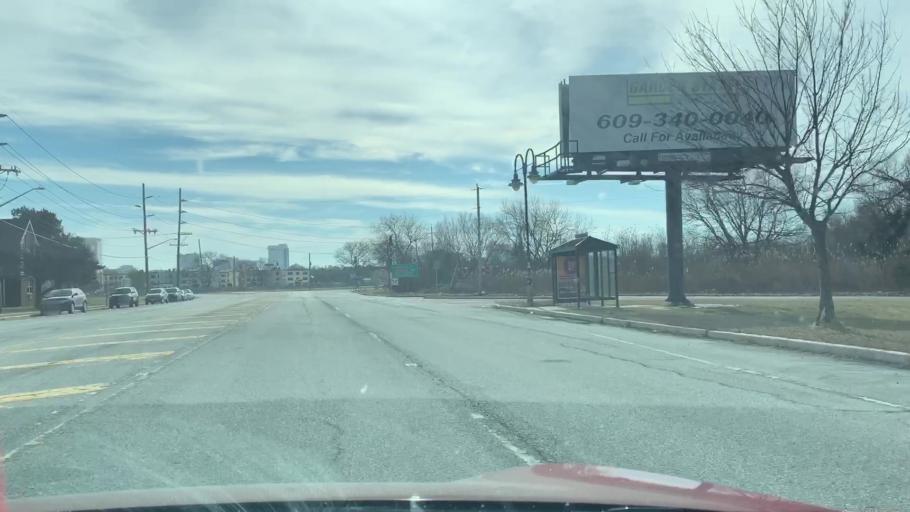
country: US
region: New Jersey
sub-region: Atlantic County
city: Atlantic City
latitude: 39.3736
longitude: -74.4320
